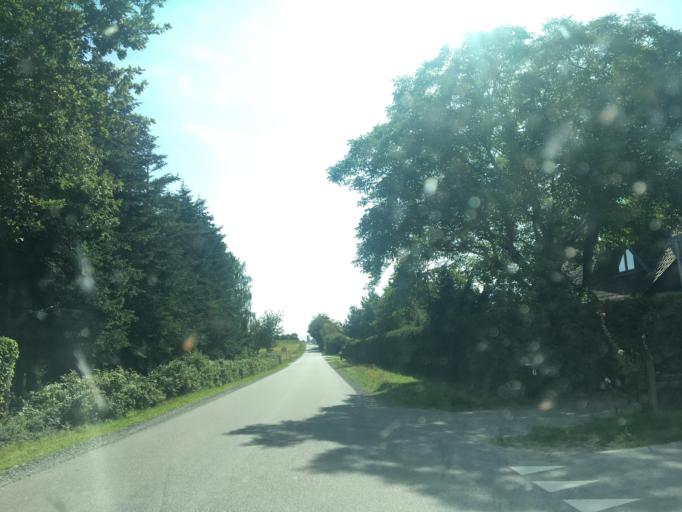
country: DK
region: South Denmark
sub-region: Middelfart Kommune
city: Strib
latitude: 55.4907
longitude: 9.7889
